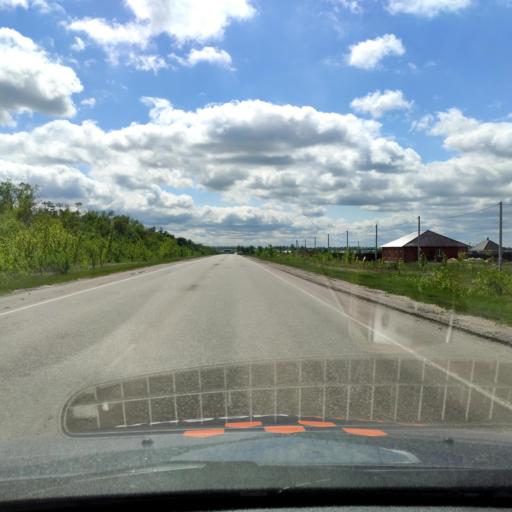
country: RU
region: Voronezj
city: Novaya Usman'
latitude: 51.6158
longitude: 39.3363
